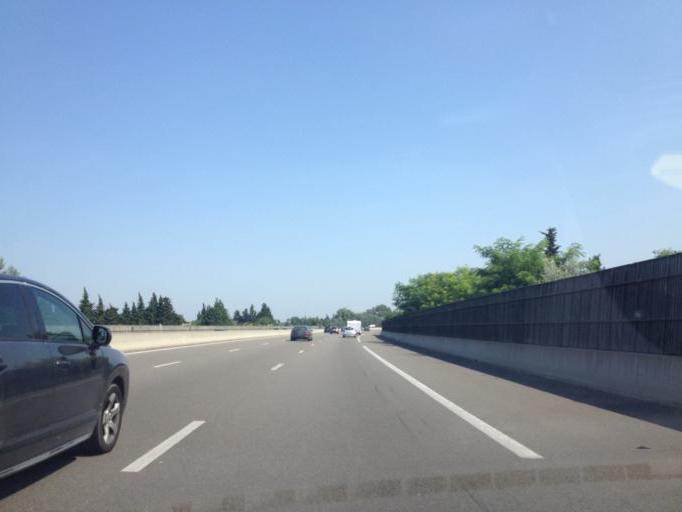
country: FR
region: Provence-Alpes-Cote d'Azur
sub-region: Departement du Vaucluse
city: Mondragon
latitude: 44.2354
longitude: 4.7072
